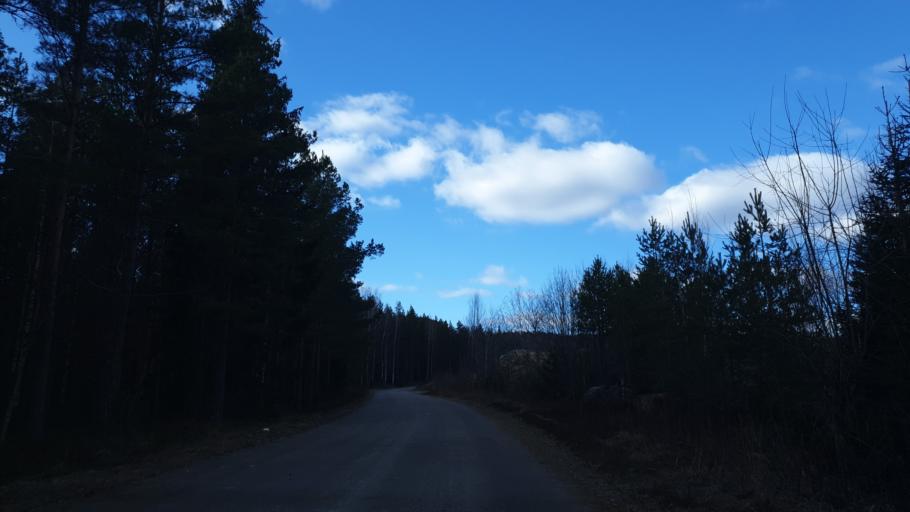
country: SE
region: OErebro
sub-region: Orebro Kommun
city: Garphyttan
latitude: 59.3555
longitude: 14.9804
